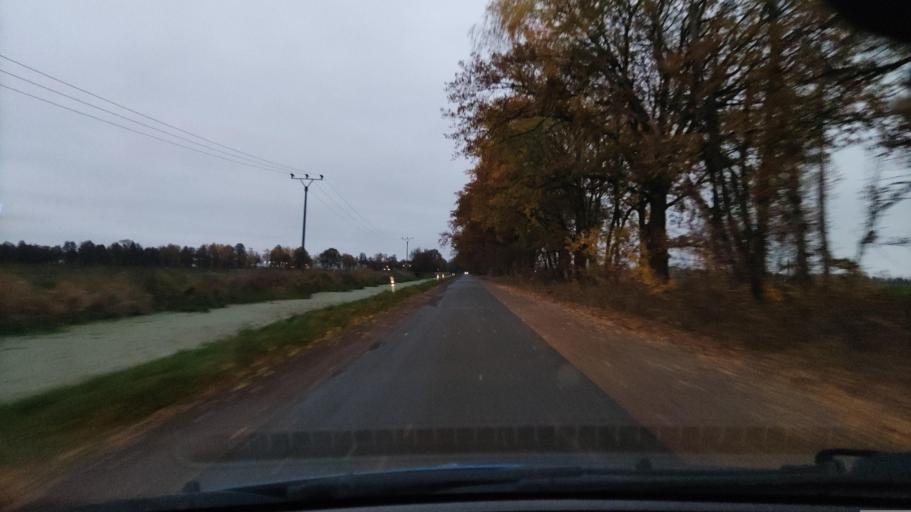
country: DE
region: Mecklenburg-Vorpommern
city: Neu Kaliss
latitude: 53.1831
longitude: 11.2637
